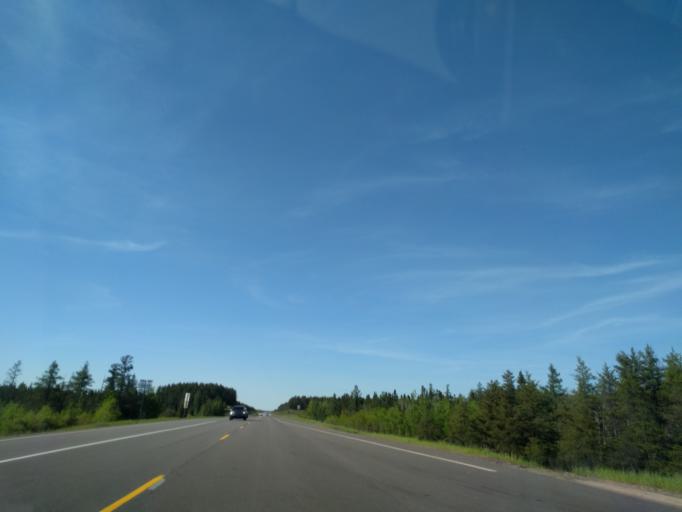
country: US
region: Michigan
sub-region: Marquette County
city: K. I. Sawyer Air Force Base
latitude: 46.3170
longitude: -87.4175
